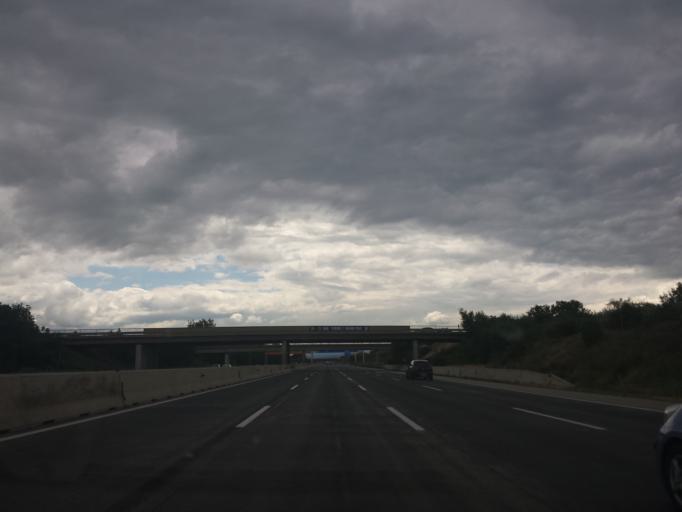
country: AT
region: Lower Austria
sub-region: Politischer Bezirk Baden
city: Traiskirchen
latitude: 48.0077
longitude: 16.3109
